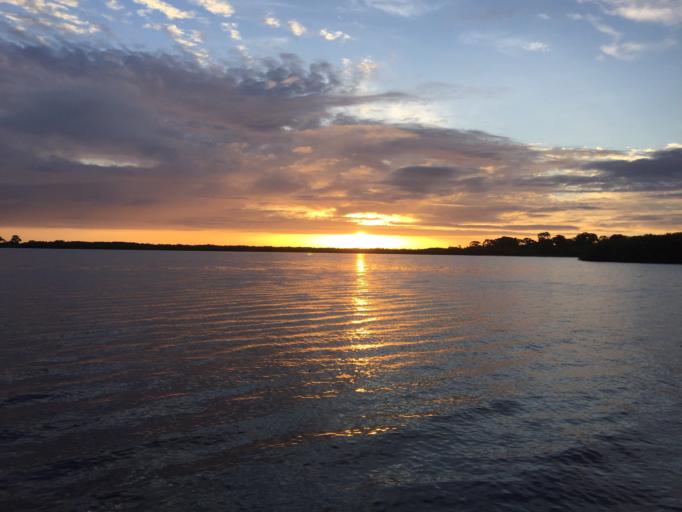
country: SN
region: Fatick
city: Sokone
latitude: 13.8309
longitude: -16.4923
